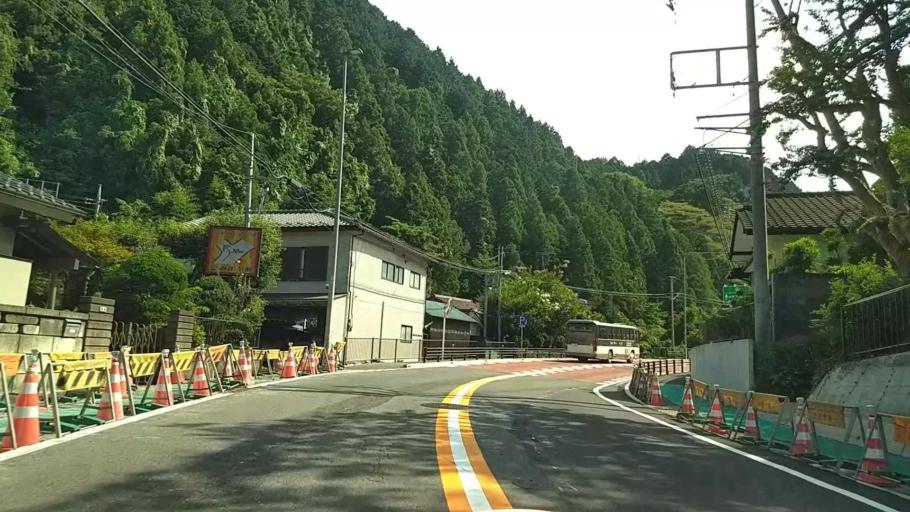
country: JP
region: Tokyo
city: Hachioji
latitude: 35.6184
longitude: 139.2626
